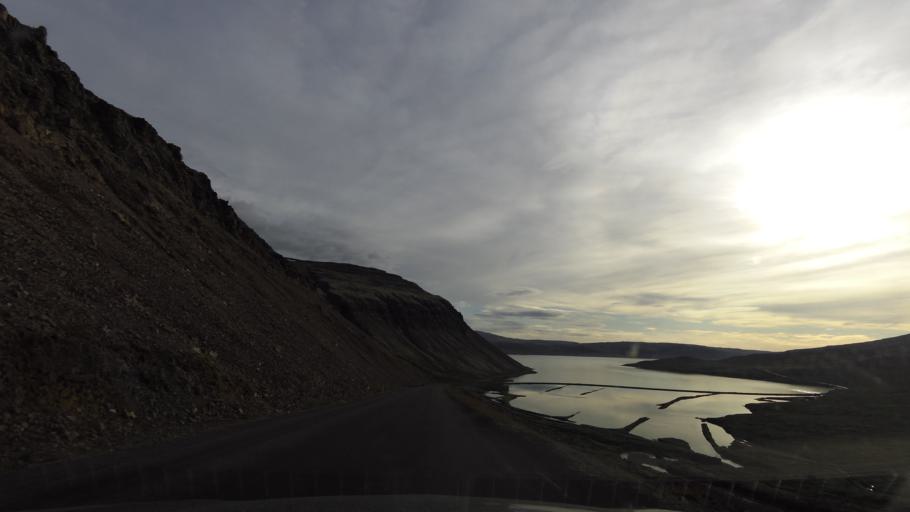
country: IS
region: West
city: Olafsvik
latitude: 65.5331
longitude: -23.7607
